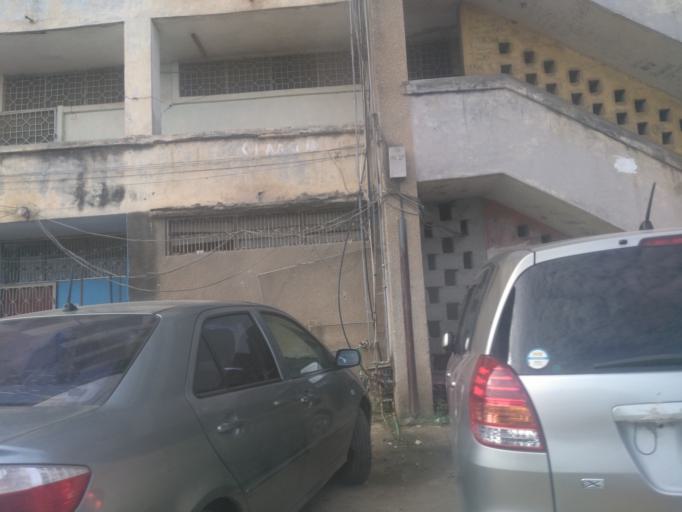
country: TZ
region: Zanzibar Urban/West
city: Zanzibar
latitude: -6.1644
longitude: 39.2009
